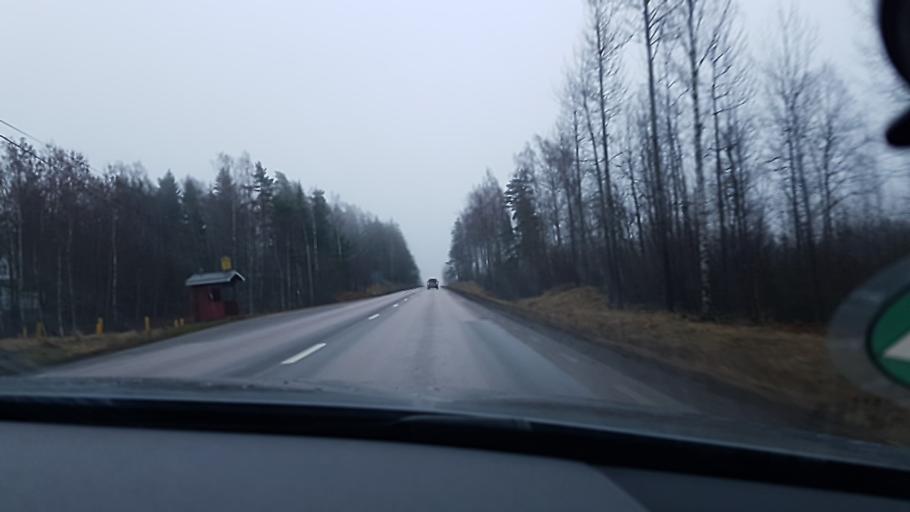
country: SE
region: Vaermland
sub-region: Kristinehamns Kommun
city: Kristinehamn
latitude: 59.2808
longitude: 14.1490
